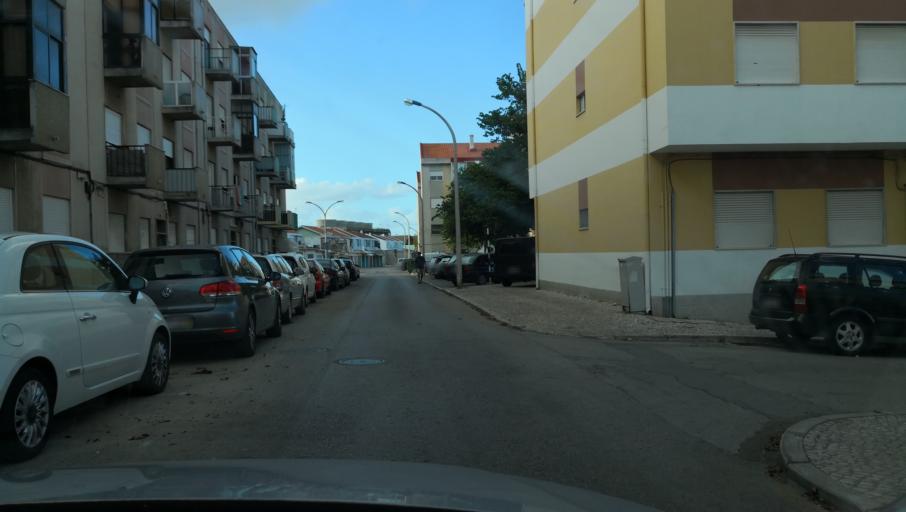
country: PT
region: Setubal
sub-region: Barreiro
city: Barreiro
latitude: 38.6695
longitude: -9.0483
